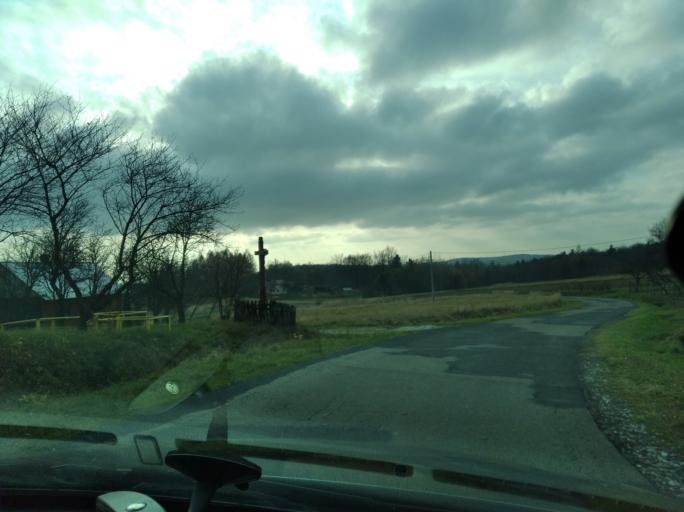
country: PL
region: Subcarpathian Voivodeship
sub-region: Powiat przemyski
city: Przedmiescie Dubieckie
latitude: 49.8876
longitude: 22.3732
